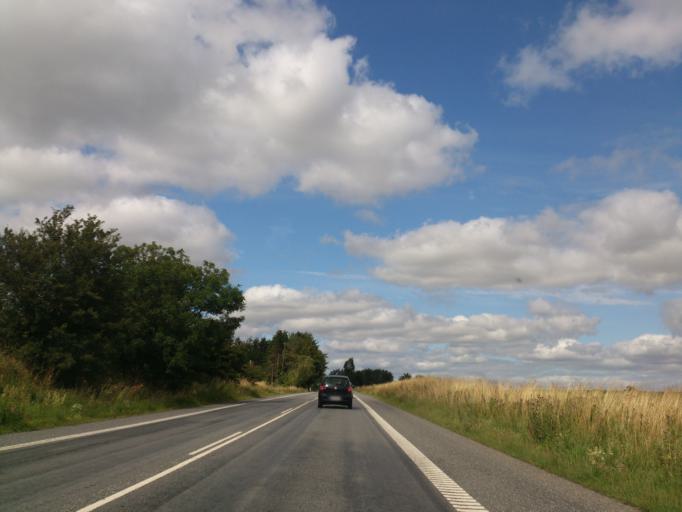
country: DK
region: South Denmark
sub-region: Aabenraa Kommune
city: Krusa
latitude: 54.9062
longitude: 9.4391
